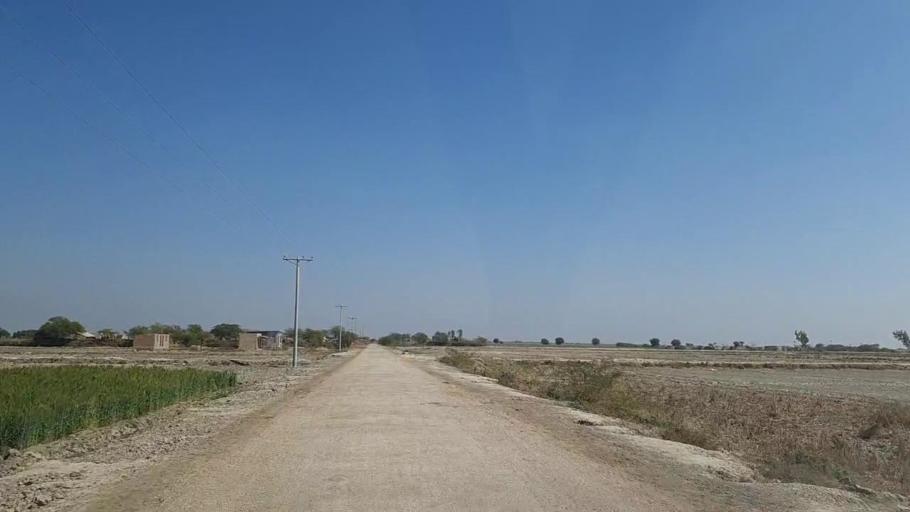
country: PK
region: Sindh
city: Pithoro
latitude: 25.4165
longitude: 69.4141
